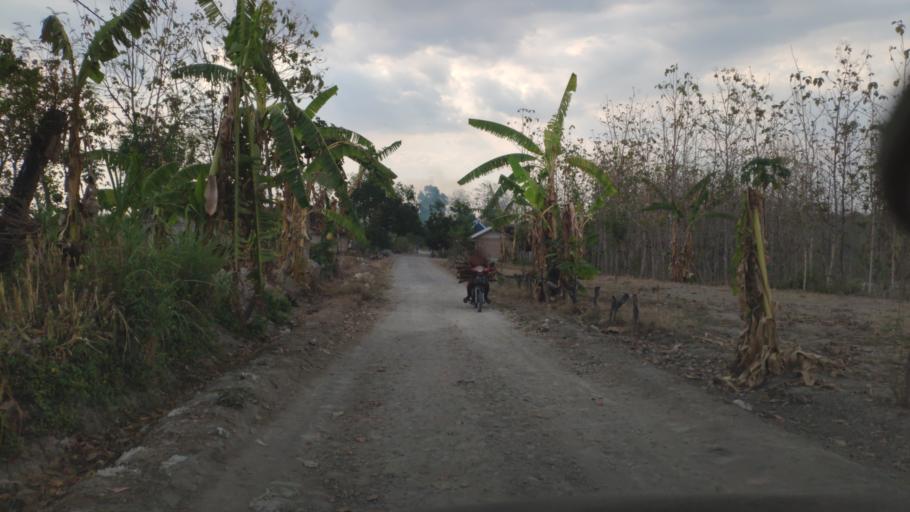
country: ID
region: Central Java
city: Randublatung
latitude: -7.2886
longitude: 111.3063
